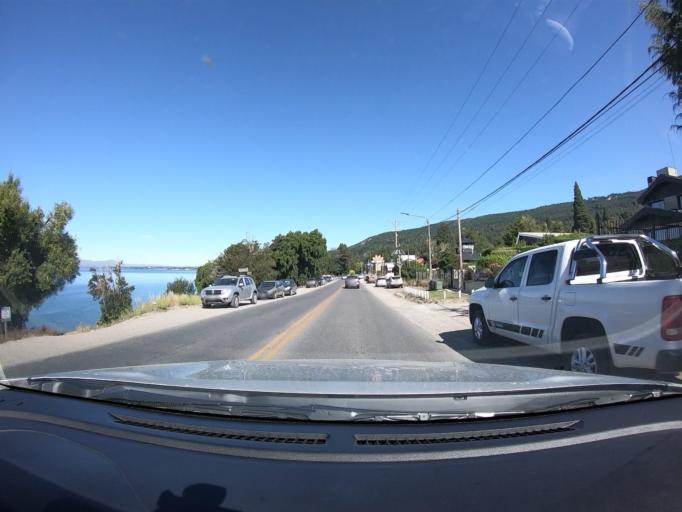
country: AR
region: Rio Negro
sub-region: Departamento de Bariloche
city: San Carlos de Bariloche
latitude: -41.1263
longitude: -71.3539
